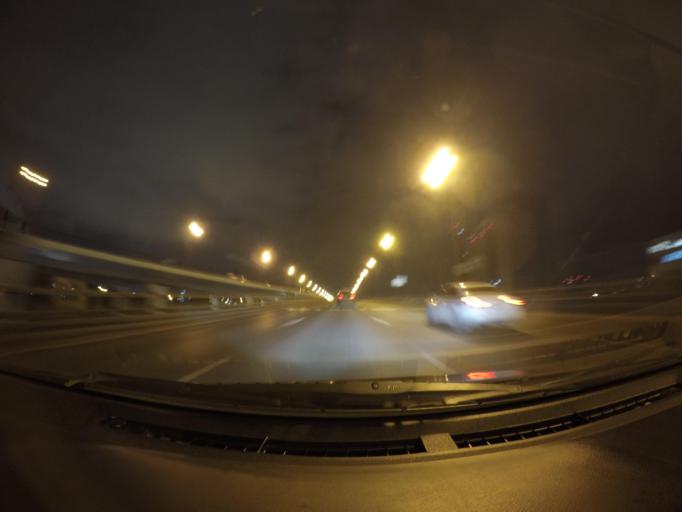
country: RU
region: Moscow
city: Tekstil'shchiki
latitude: 55.7253
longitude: 37.7122
